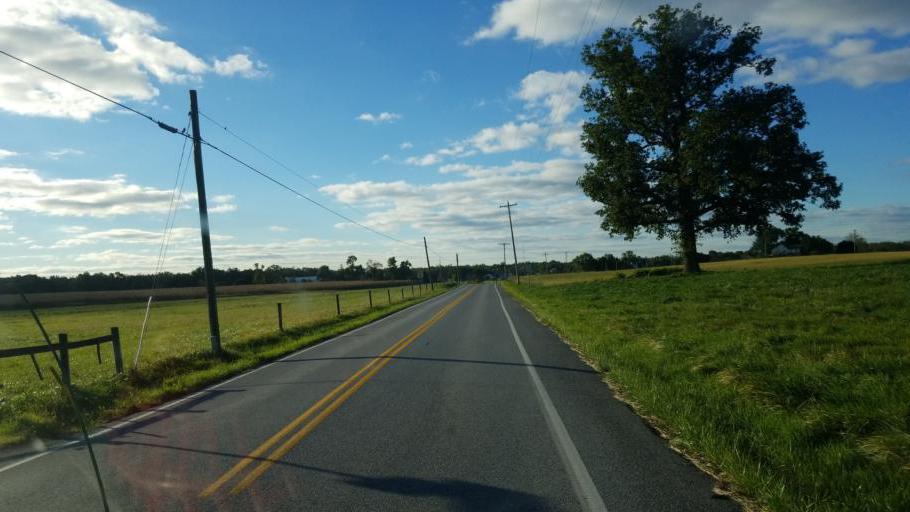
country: US
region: Pennsylvania
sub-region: Adams County
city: Gettysburg
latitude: 39.8638
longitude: -77.2283
